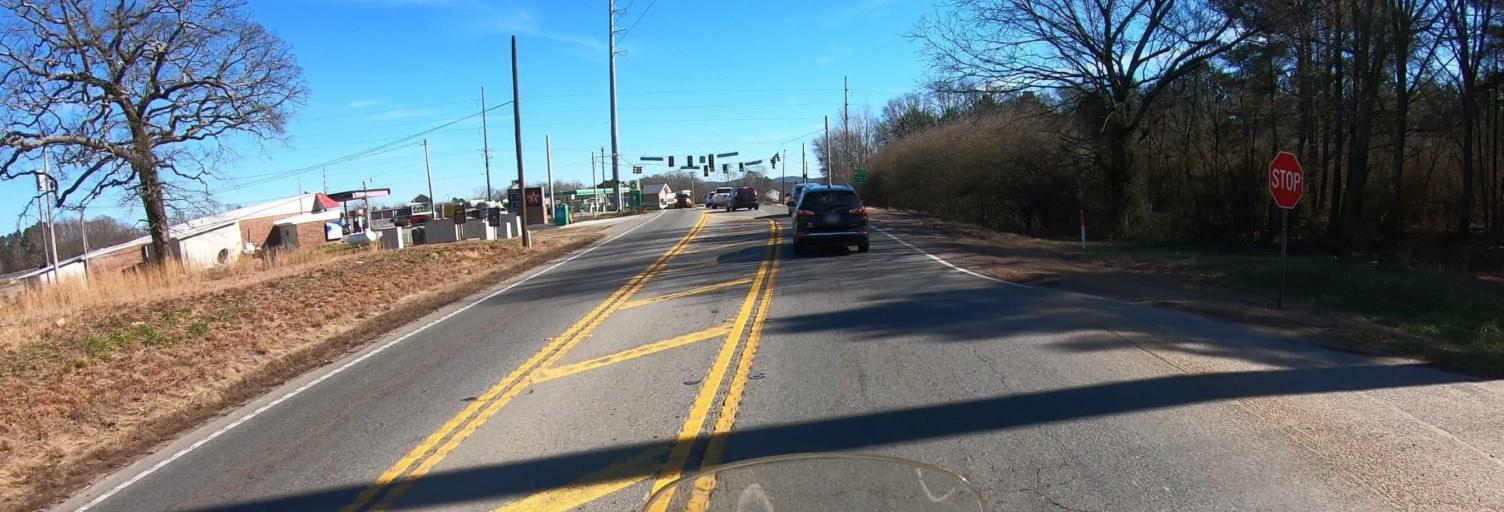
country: US
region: Georgia
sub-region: Forsyth County
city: Cumming
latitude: 34.2951
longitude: -84.1576
